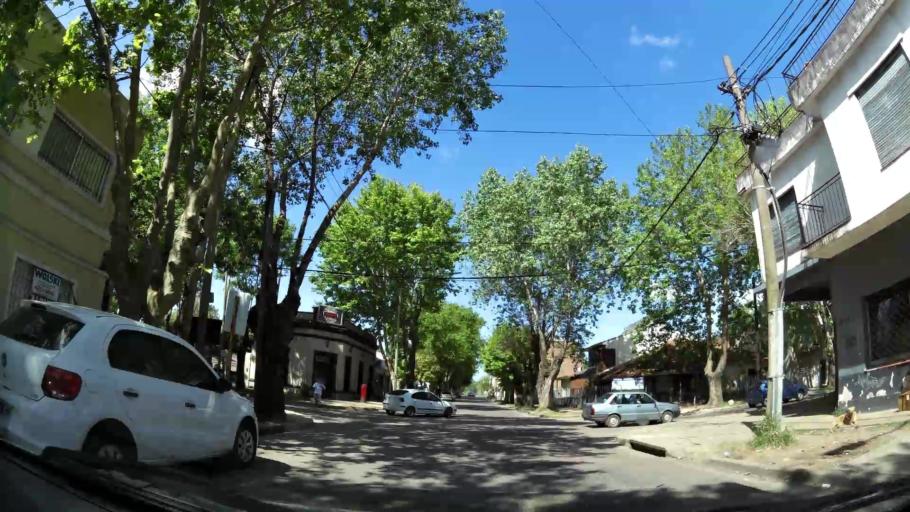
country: AR
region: Buenos Aires
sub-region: Partido de Quilmes
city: Quilmes
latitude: -34.8076
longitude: -58.2717
